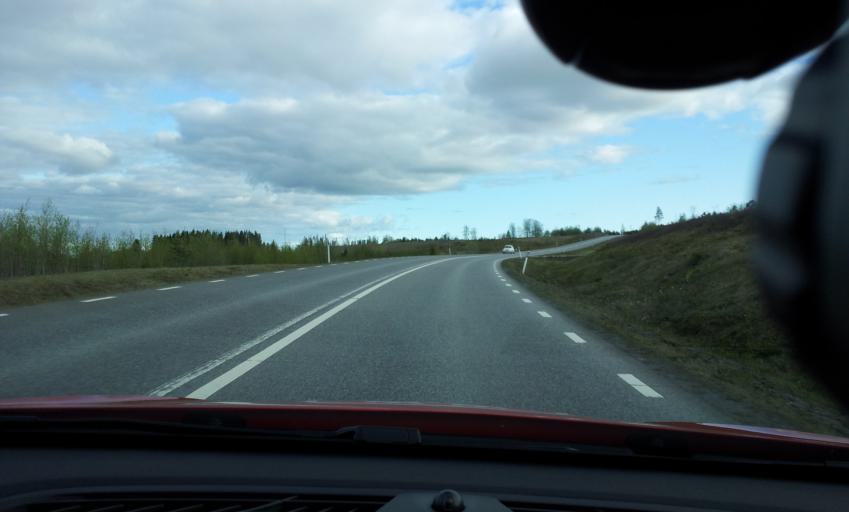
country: SE
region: Jaemtland
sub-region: OEstersunds Kommun
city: Ostersund
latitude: 63.1868
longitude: 14.5354
